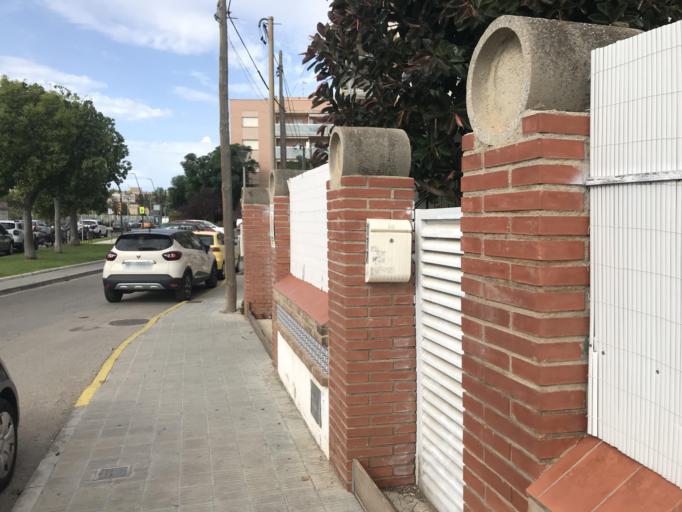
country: ES
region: Catalonia
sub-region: Provincia de Tarragona
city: Torredembarra
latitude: 41.1434
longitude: 1.4061
